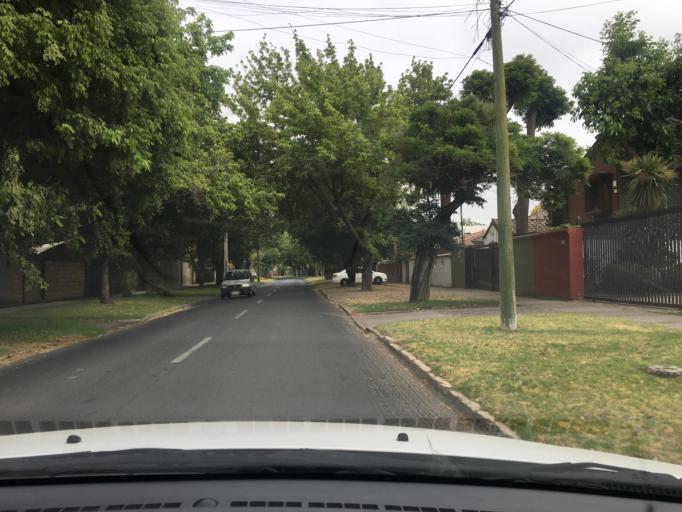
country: CL
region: Santiago Metropolitan
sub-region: Provincia de Santiago
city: Villa Presidente Frei, Nunoa, Santiago, Chile
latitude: -33.4501
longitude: -70.5585
